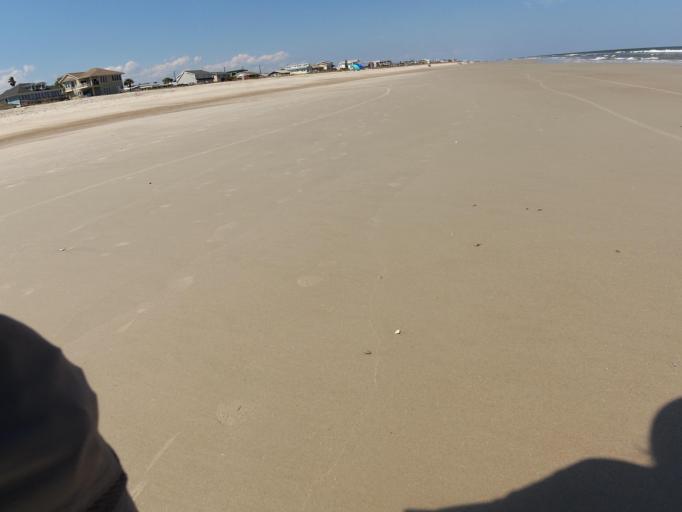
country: US
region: Florida
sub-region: Nassau County
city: Fernandina Beach
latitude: 30.6497
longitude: -81.4328
